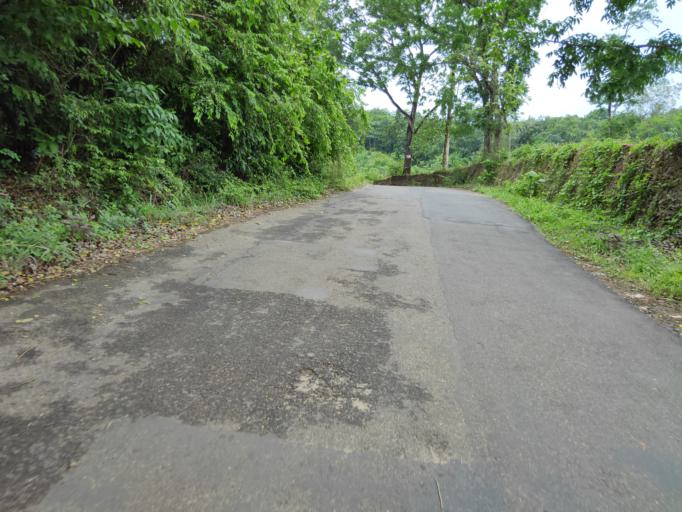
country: IN
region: Kerala
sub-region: Malappuram
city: Manjeri
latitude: 11.2354
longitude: 76.2487
